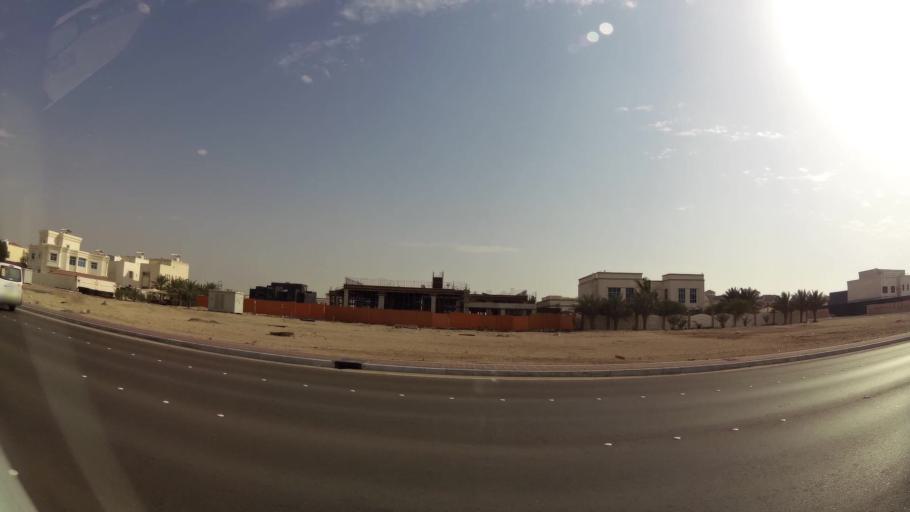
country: AE
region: Abu Dhabi
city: Abu Dhabi
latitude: 24.3259
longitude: 54.5678
